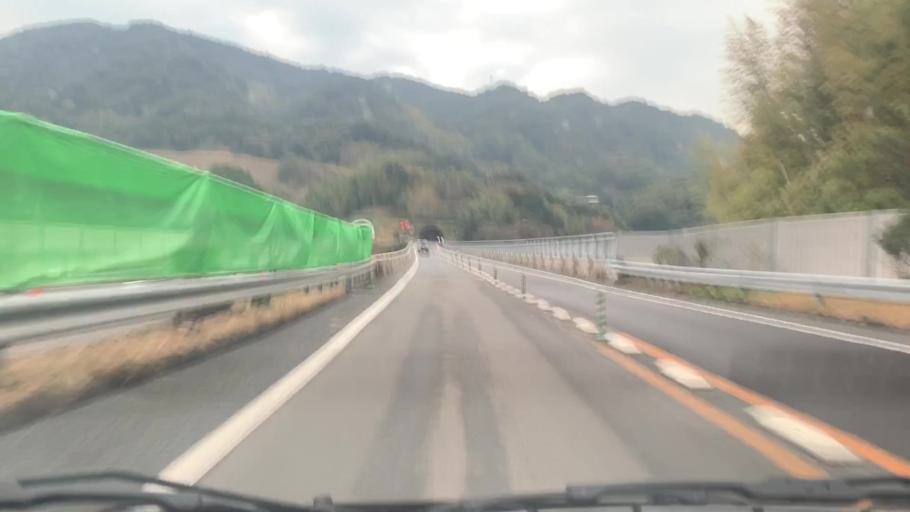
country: JP
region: Nagasaki
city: Obita
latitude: 32.8017
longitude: 129.9653
